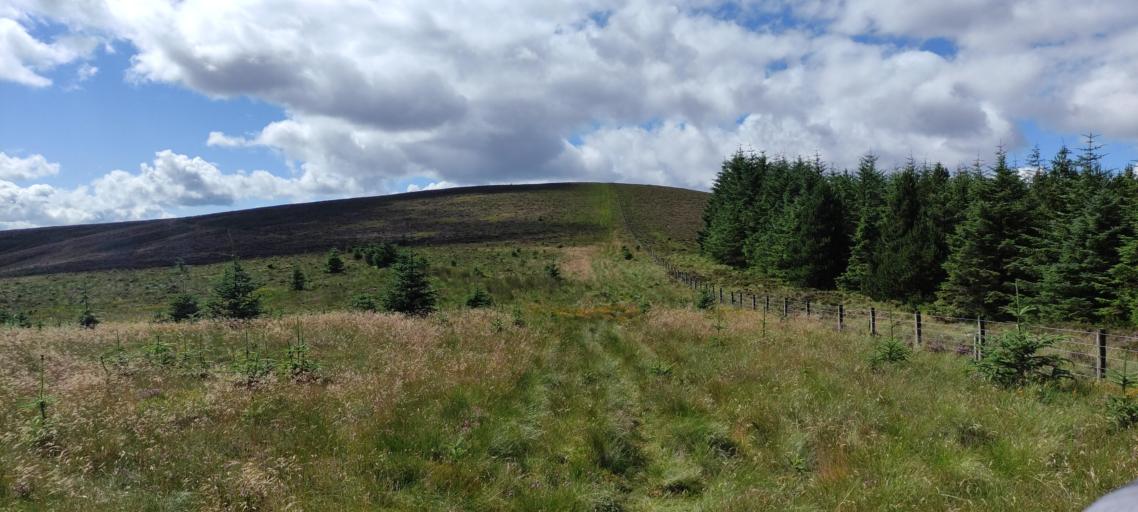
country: GB
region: Scotland
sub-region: Dumfries and Galloway
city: Langholm
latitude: 55.2423
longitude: -3.0357
